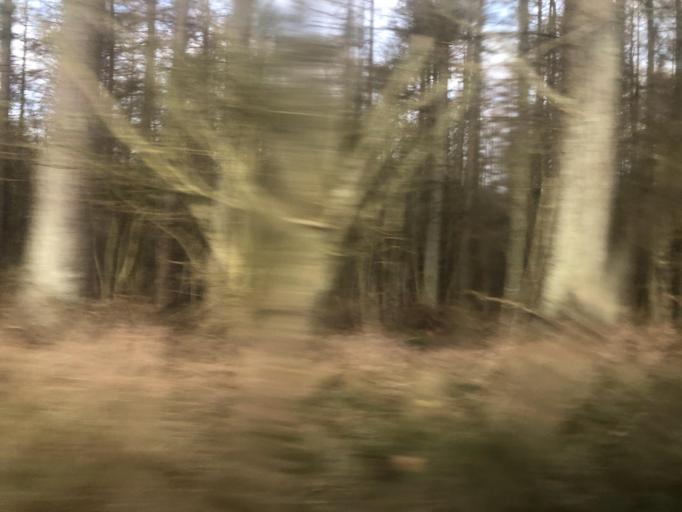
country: SE
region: Skane
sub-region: Lunds Kommun
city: Veberod
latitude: 55.6065
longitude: 13.5375
